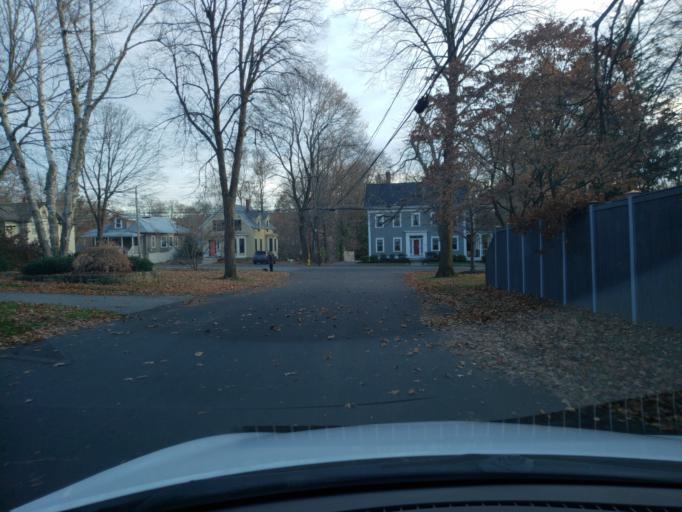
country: US
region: Massachusetts
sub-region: Essex County
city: Andover
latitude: 42.6592
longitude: -71.1344
